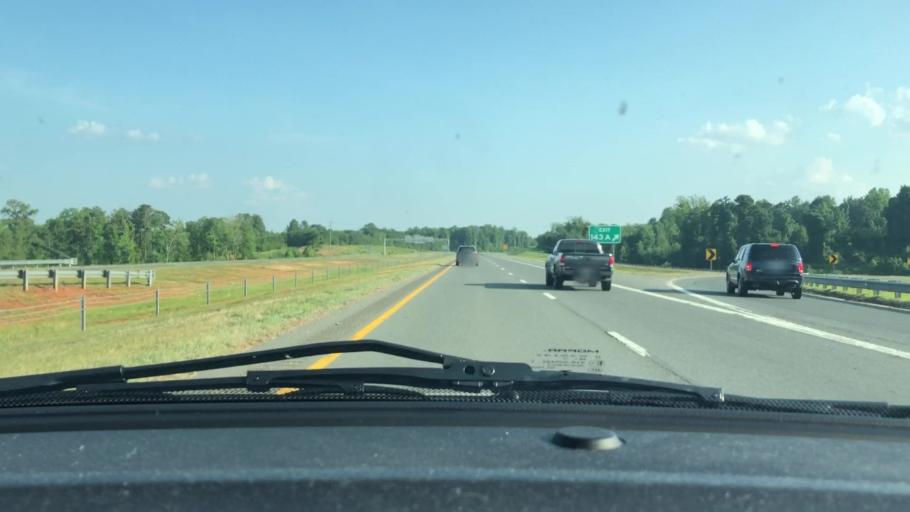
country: US
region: North Carolina
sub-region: Lee County
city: Broadway
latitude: 35.4463
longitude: -79.1195
